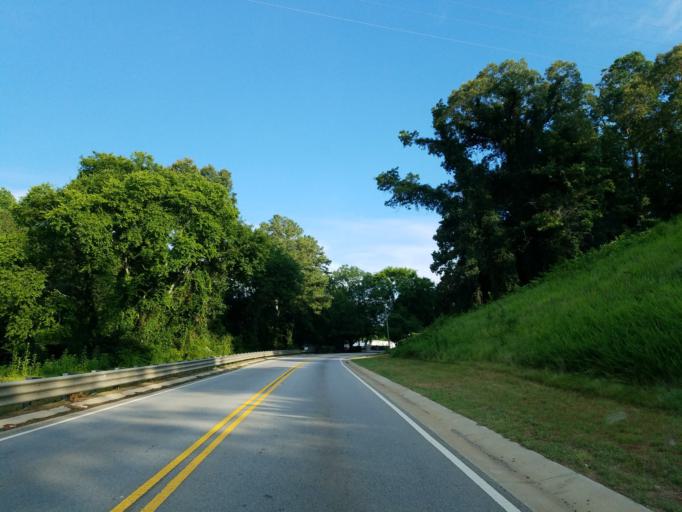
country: US
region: Georgia
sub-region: Bartow County
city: Emerson
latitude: 34.1315
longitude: -84.7584
